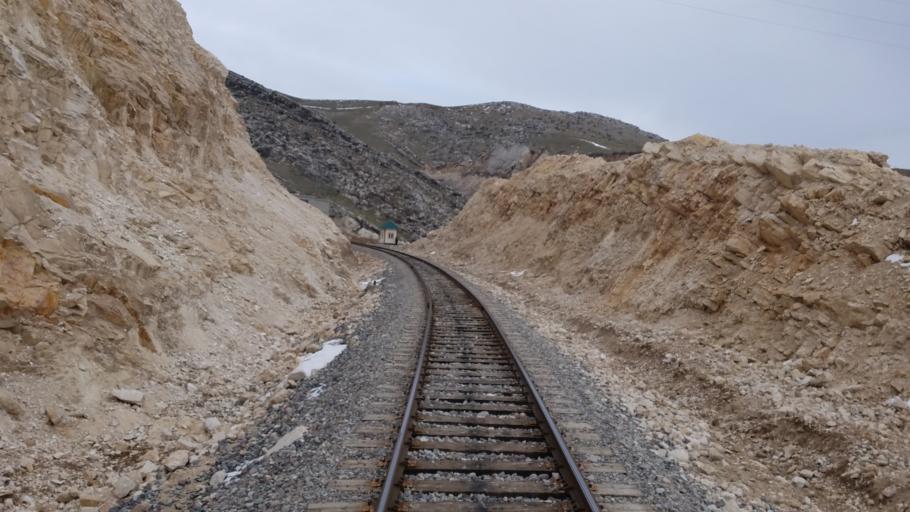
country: TJ
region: Khatlon
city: Yovon
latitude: 38.3951
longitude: 68.9654
